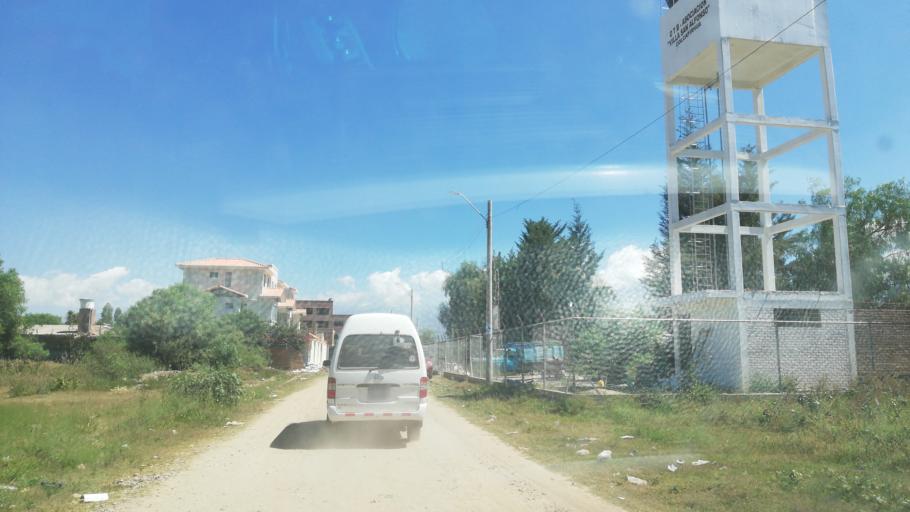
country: BO
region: Cochabamba
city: Cochabamba
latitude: -17.3763
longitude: -66.2092
